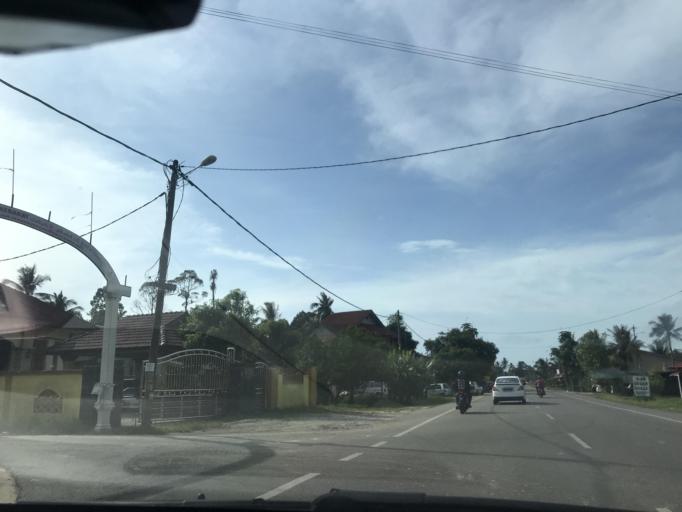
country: MY
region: Kelantan
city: Kota Bharu
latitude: 6.1357
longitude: 102.2027
